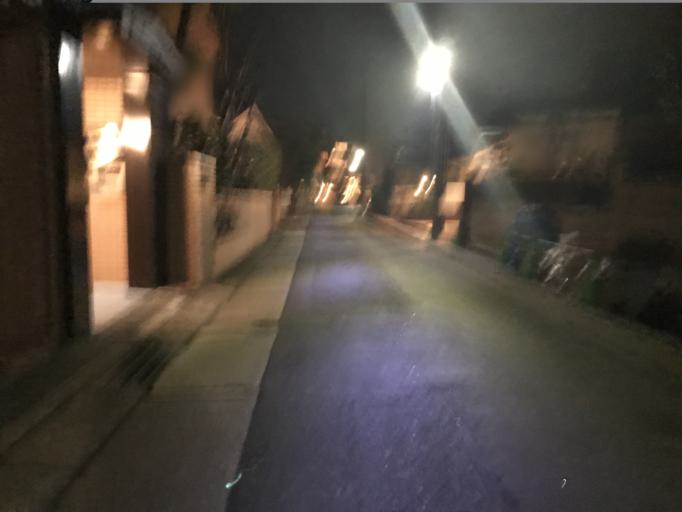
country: JP
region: Aichi
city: Nagoya-shi
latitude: 35.1346
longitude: 136.9683
